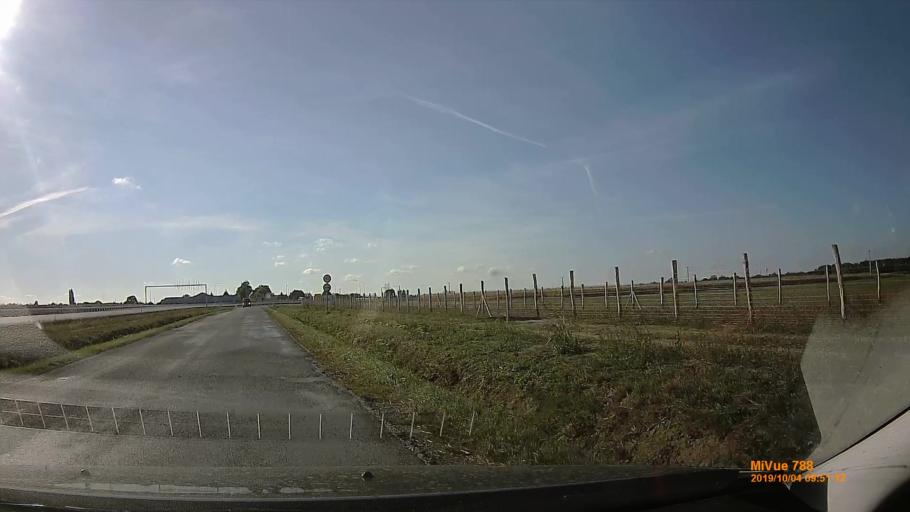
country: HU
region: Somogy
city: Kaposvar
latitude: 46.4284
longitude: 17.7738
